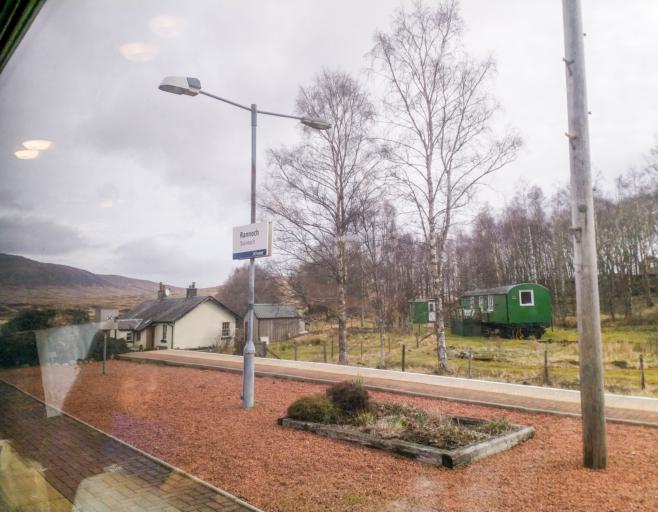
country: GB
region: Scotland
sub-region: Highland
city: Spean Bridge
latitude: 56.6863
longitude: -4.5769
